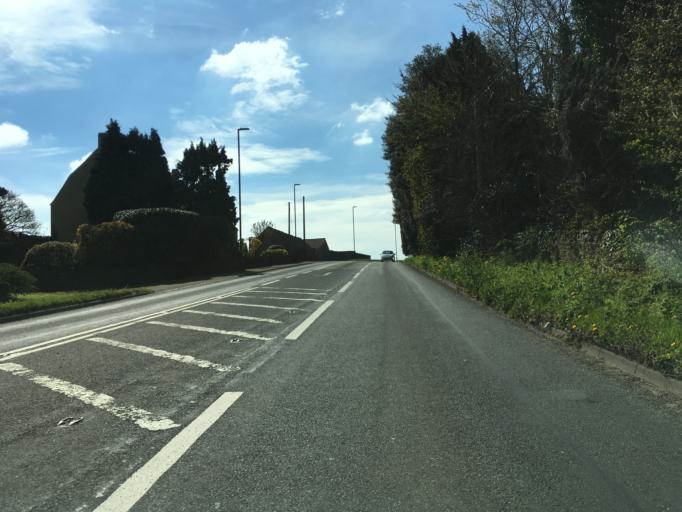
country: GB
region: England
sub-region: South Gloucestershire
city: Thornbury
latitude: 51.5988
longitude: -2.5025
